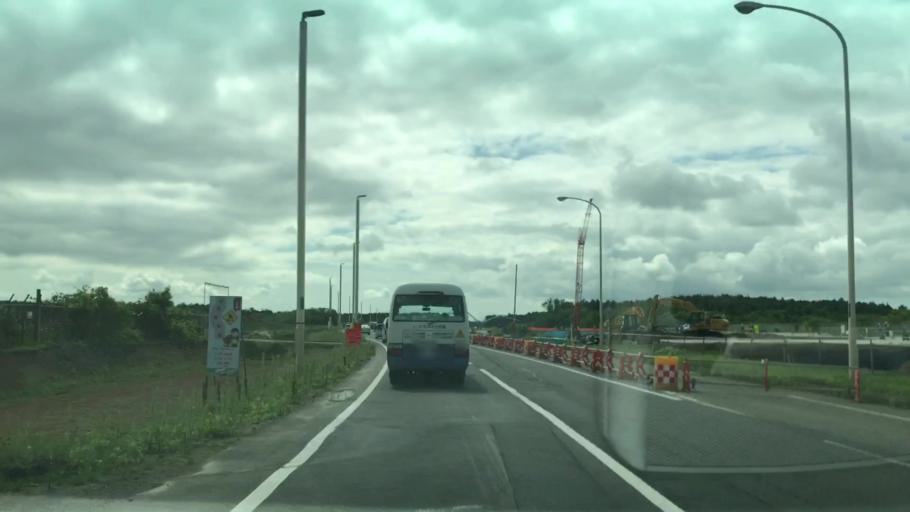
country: JP
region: Hokkaido
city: Chitose
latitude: 42.7786
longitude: 141.6782
